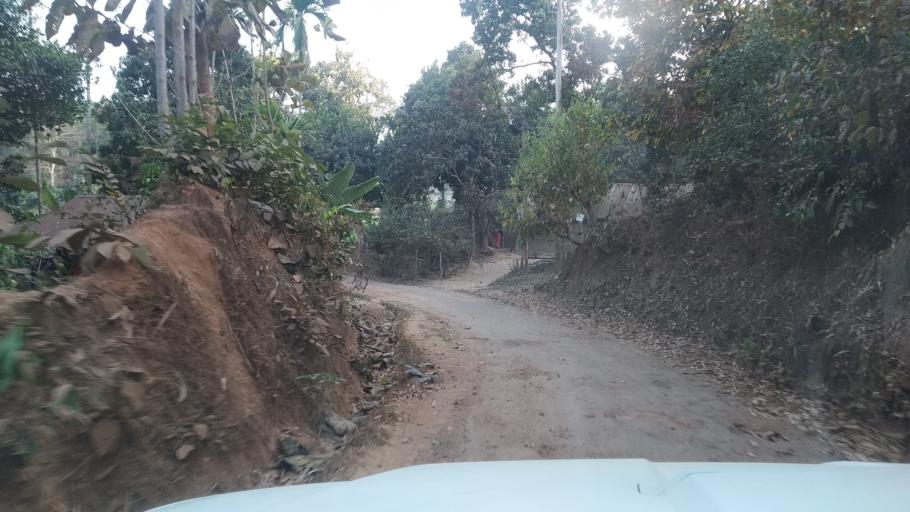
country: IN
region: Tripura
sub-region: South Tripura
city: Belonia
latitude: 23.3155
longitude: 91.3255
